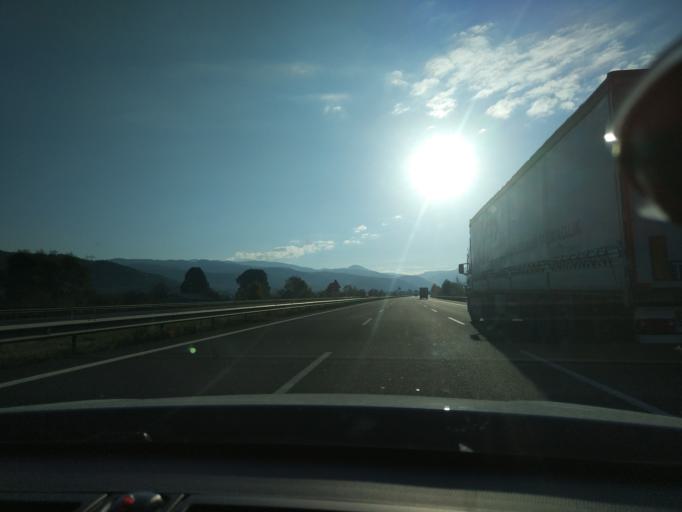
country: TR
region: Duzce
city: Kaynasli
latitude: 40.7821
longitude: 31.3150
